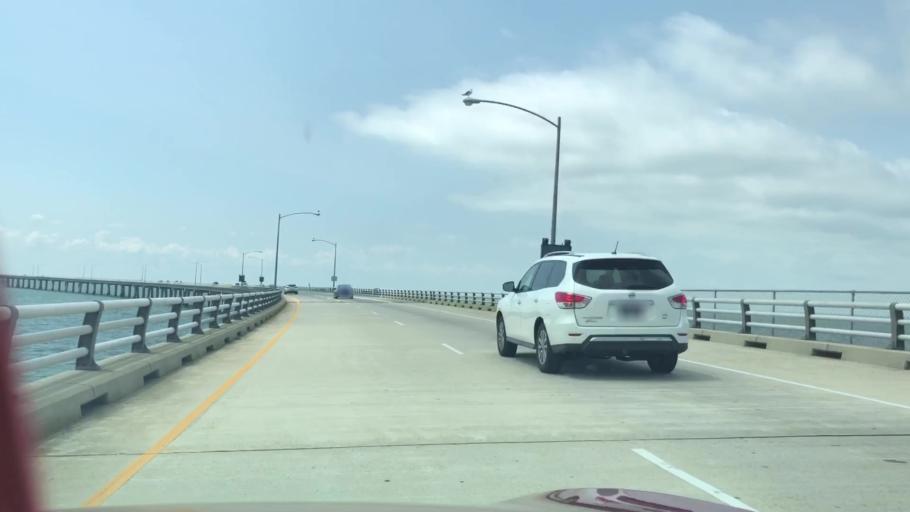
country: US
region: Virginia
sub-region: City of Virginia Beach
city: Virginia Beach
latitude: 37.0325
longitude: -76.0839
